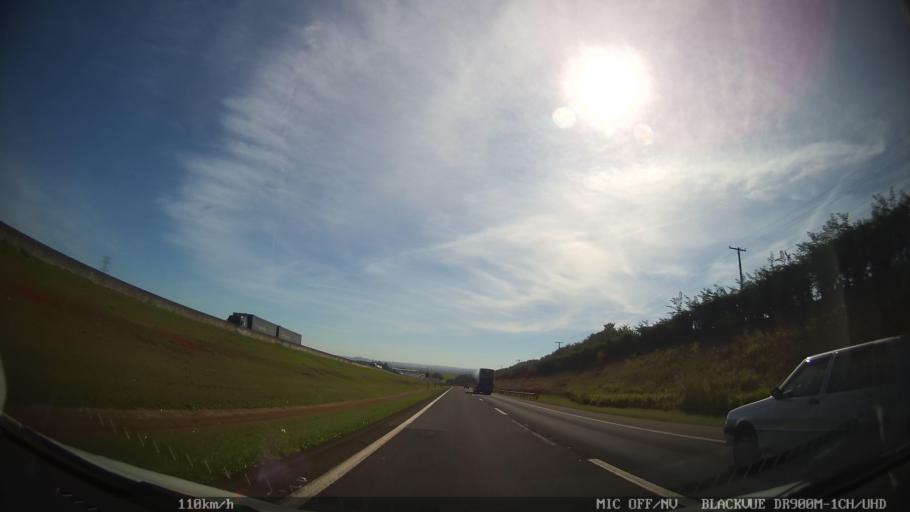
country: BR
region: Sao Paulo
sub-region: Leme
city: Leme
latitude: -22.2589
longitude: -47.3901
